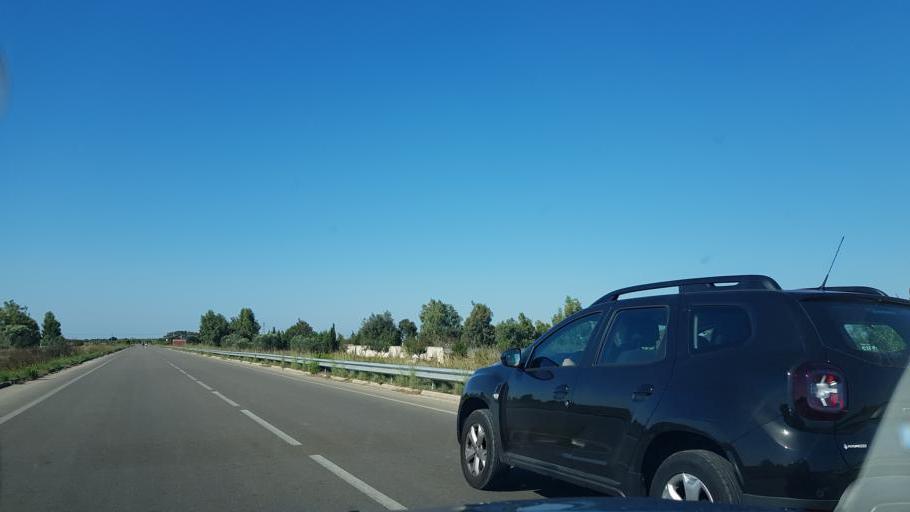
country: IT
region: Apulia
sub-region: Provincia di Lecce
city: Carmiano
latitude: 40.3131
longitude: 18.0325
